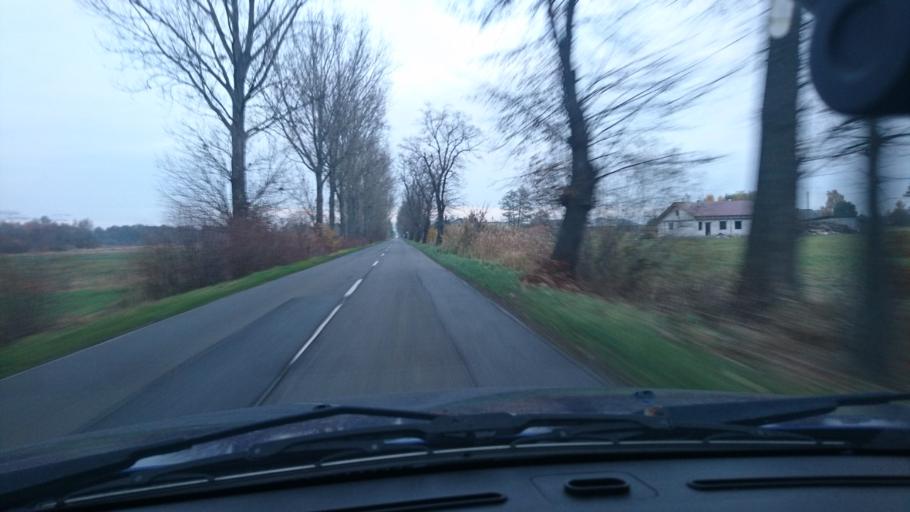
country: PL
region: Greater Poland Voivodeship
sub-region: Powiat ostrowski
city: Odolanow
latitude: 51.5465
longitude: 17.6566
